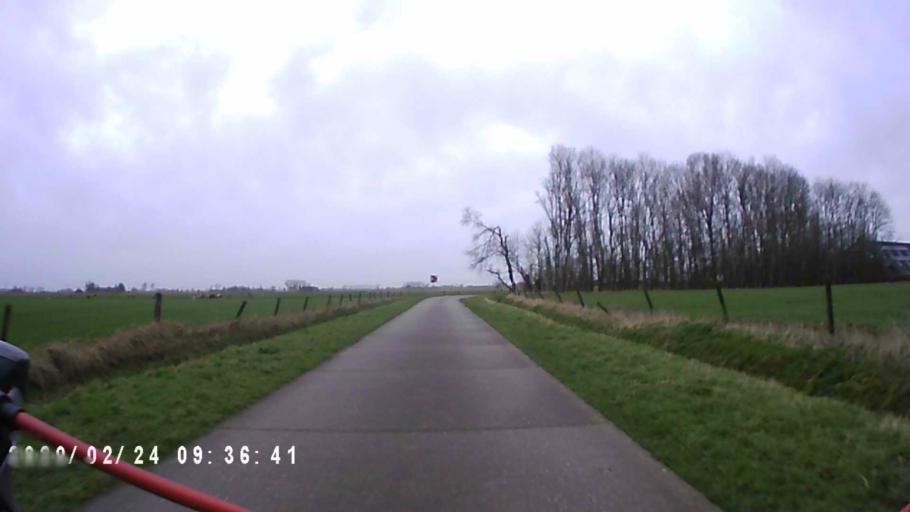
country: NL
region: Groningen
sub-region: Gemeente Winsum
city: Winsum
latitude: 53.3002
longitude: 6.5134
